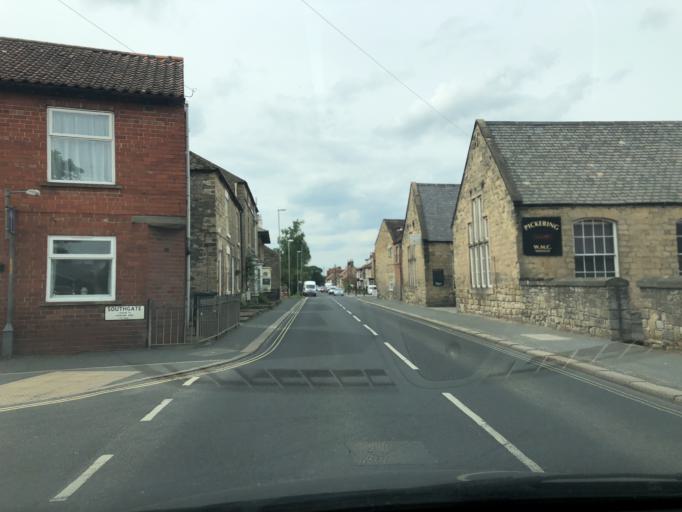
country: GB
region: England
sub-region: North Yorkshire
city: Pickering
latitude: 54.2452
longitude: -0.7820
